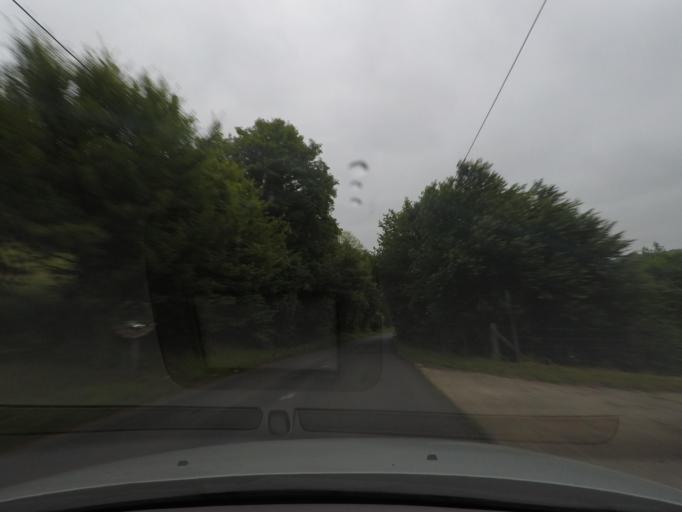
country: FR
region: Haute-Normandie
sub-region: Departement de la Seine-Maritime
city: Fontaine-le-Bourg
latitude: 49.5710
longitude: 1.1775
